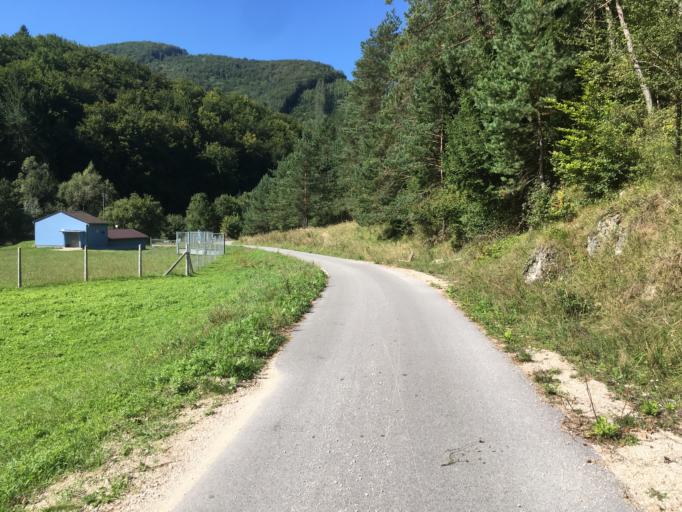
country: SK
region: Trenciansky
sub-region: Okres Povazska Bystrica
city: Povazska Bystrica
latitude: 49.0135
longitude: 18.4430
